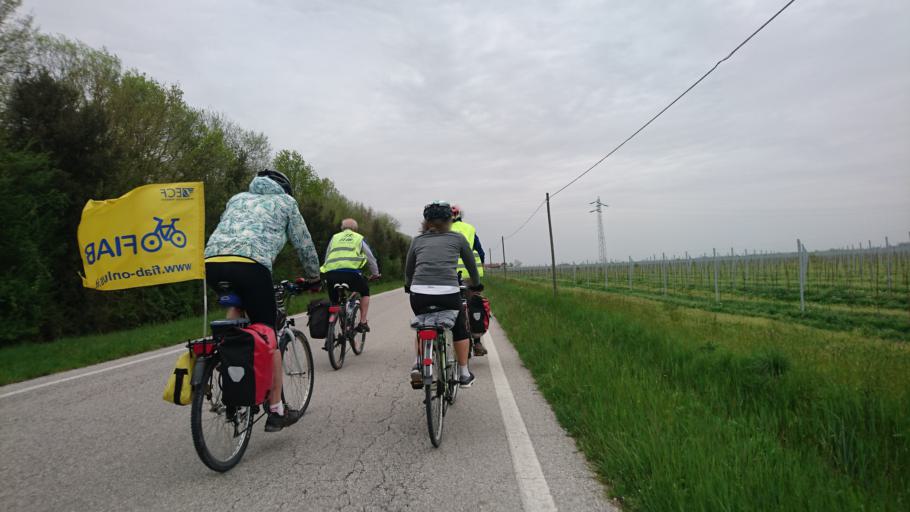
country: IT
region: Veneto
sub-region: Provincia di Venezia
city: Lugugnana
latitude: 45.6616
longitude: 12.9473
